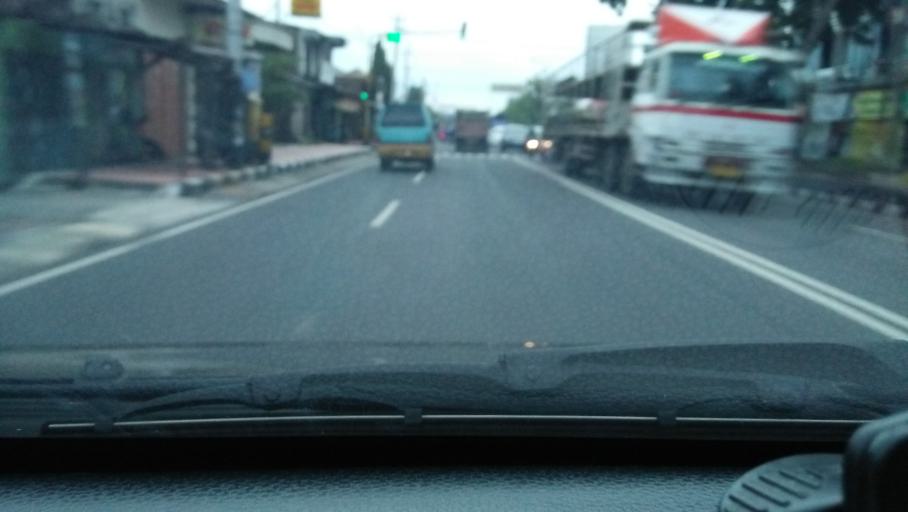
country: ID
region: Central Java
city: Magelang
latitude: -7.4462
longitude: 110.2253
